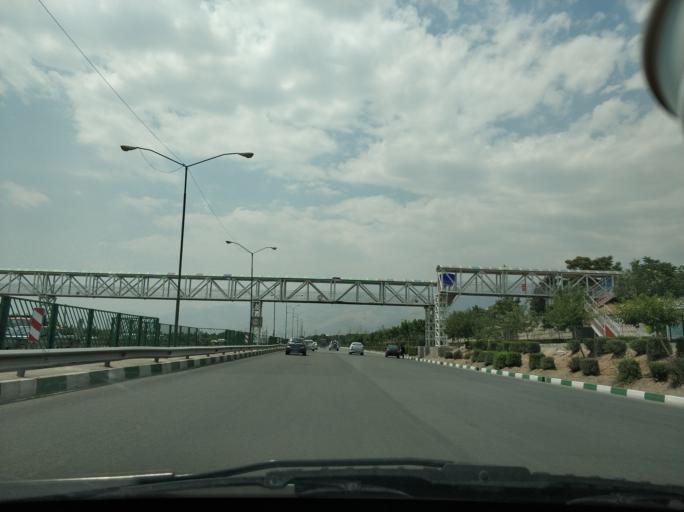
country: IR
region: Tehran
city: Tajrish
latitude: 35.7669
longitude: 51.5624
